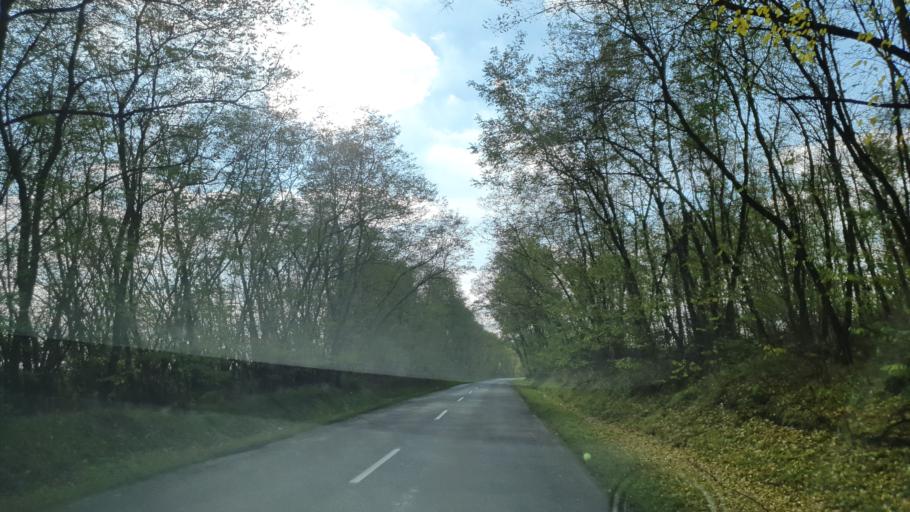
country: HU
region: Szabolcs-Szatmar-Bereg
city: Anarcs
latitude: 48.1532
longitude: 22.0940
